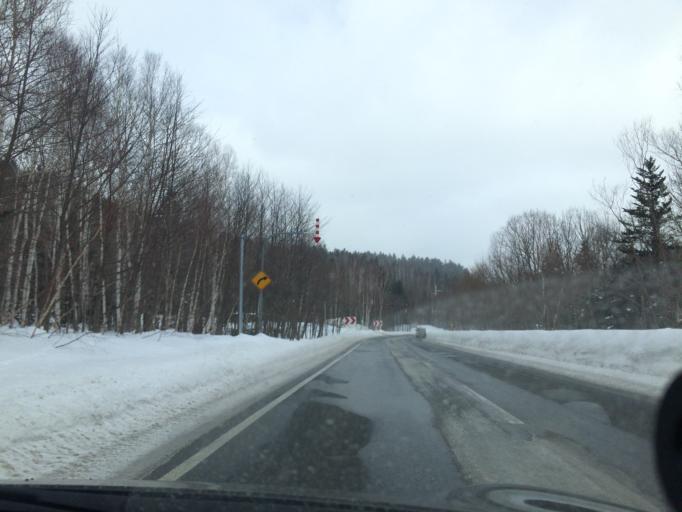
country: JP
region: Hokkaido
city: Shimo-furano
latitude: 43.0591
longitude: 142.6682
